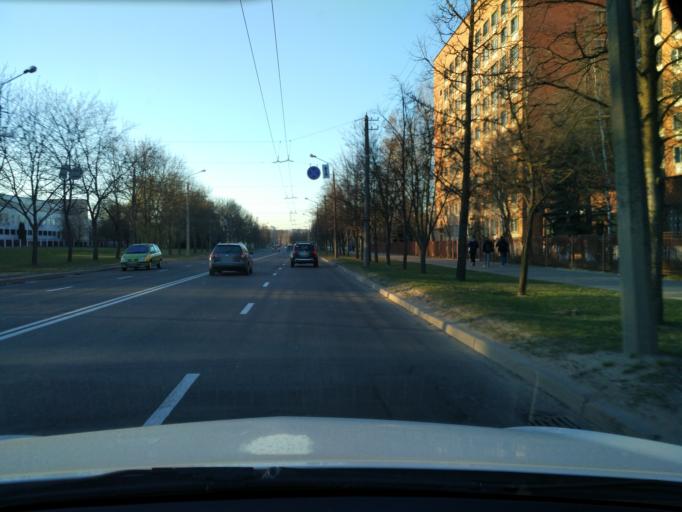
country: BY
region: Minsk
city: Syenitsa
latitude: 53.8614
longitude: 27.4973
